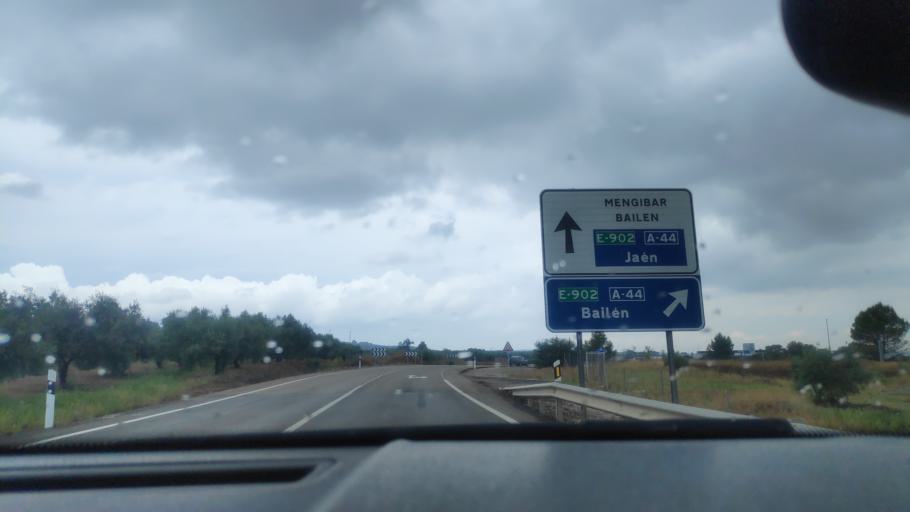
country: ES
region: Andalusia
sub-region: Provincia de Jaen
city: Jabalquinto
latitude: 38.0240
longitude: -3.7761
